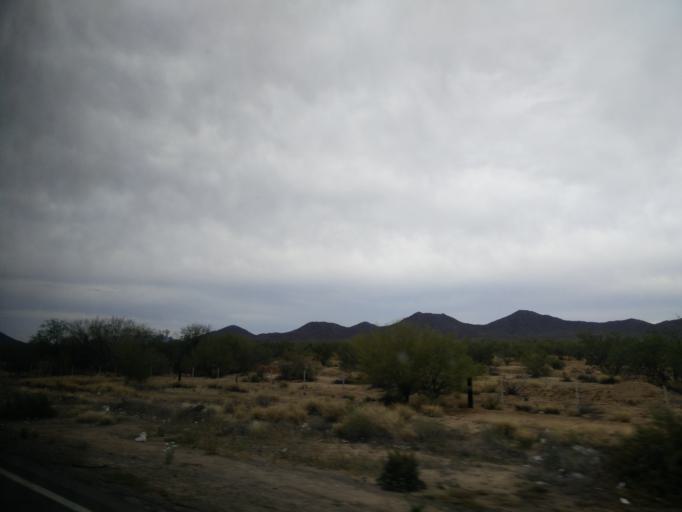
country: MX
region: Sonora
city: Hermosillo
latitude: 28.7772
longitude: -110.9652
